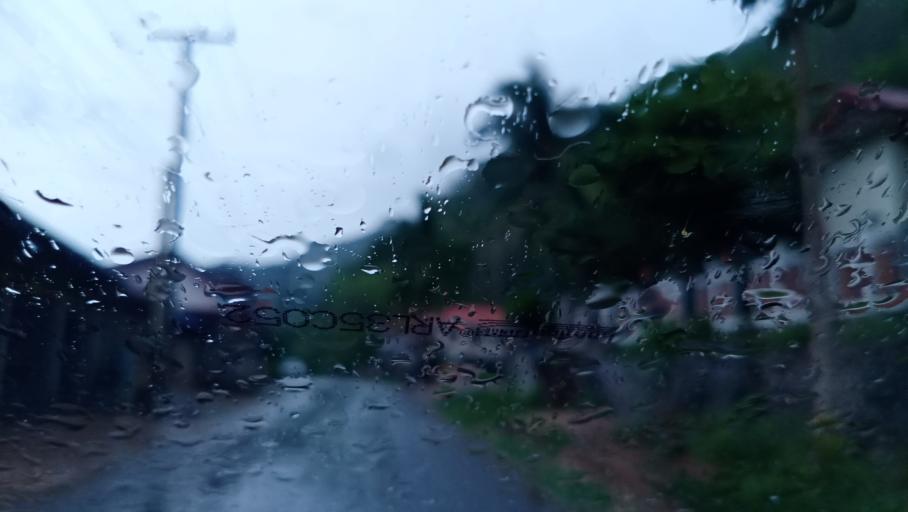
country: LA
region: Phongsali
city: Khoa
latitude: 21.0726
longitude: 102.4996
